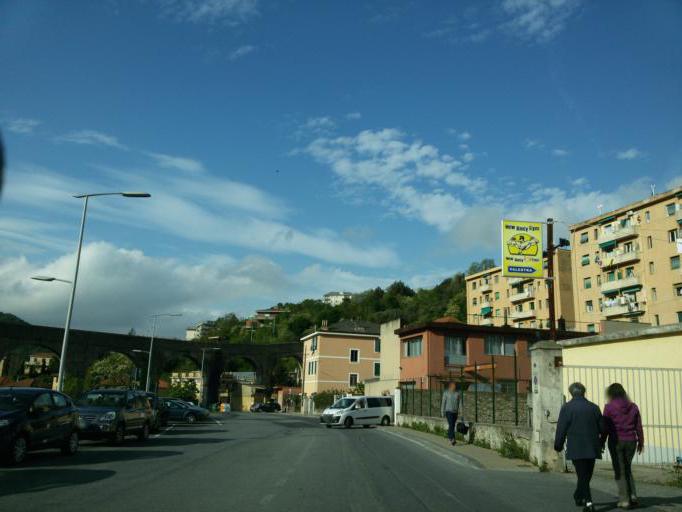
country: IT
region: Liguria
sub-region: Provincia di Genova
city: Piccarello
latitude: 44.4590
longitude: 8.9785
